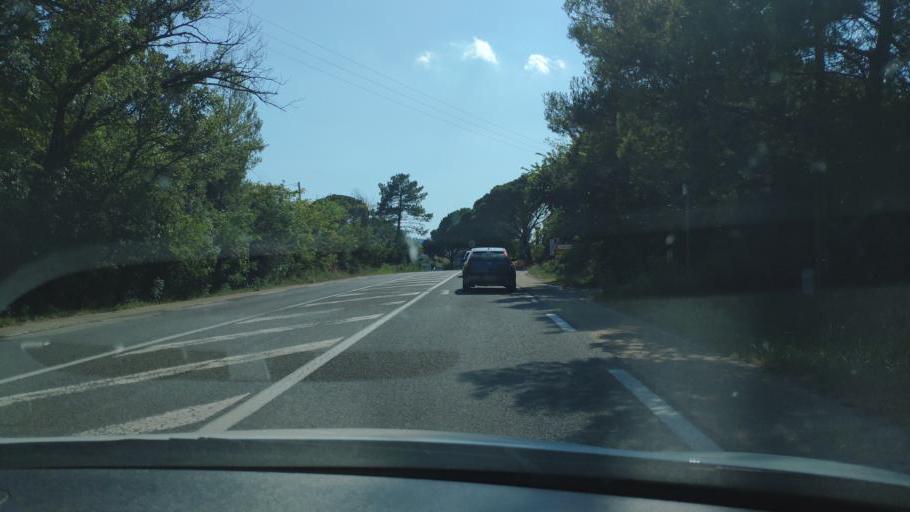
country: FR
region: Provence-Alpes-Cote d'Azur
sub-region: Departement du Var
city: Vidauban
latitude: 43.4345
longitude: 6.4408
